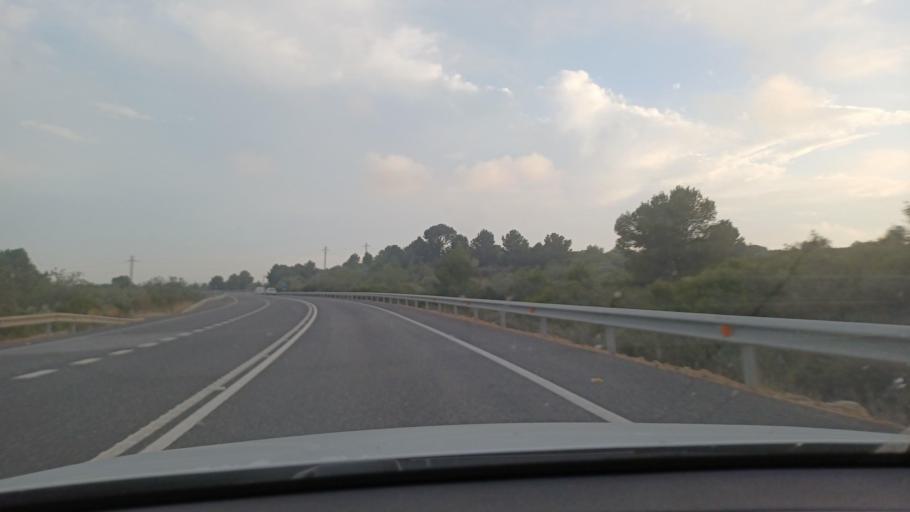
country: ES
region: Catalonia
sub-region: Provincia de Tarragona
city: El Perello
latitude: 40.8440
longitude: 0.7098
